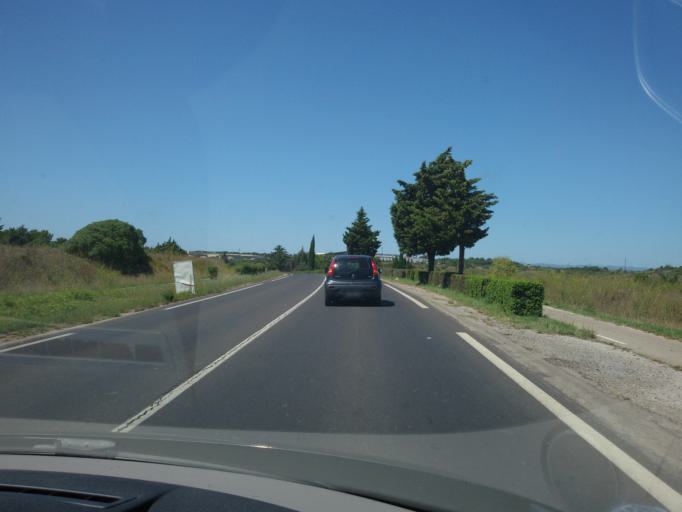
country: FR
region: Languedoc-Roussillon
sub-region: Departement de l'Herault
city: Villeneuve-les-Maguelone
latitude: 43.5433
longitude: 3.8456
